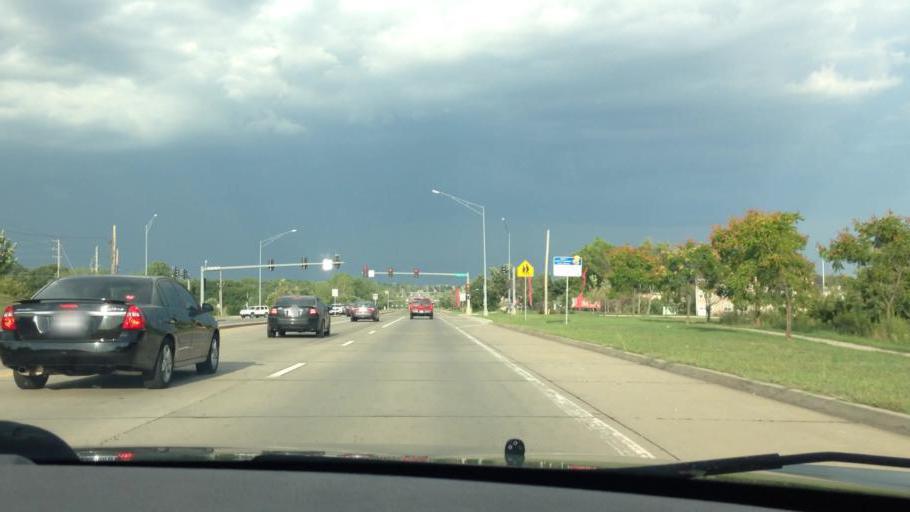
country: US
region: Missouri
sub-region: Platte County
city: Parkville
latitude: 39.2105
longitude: -94.6598
